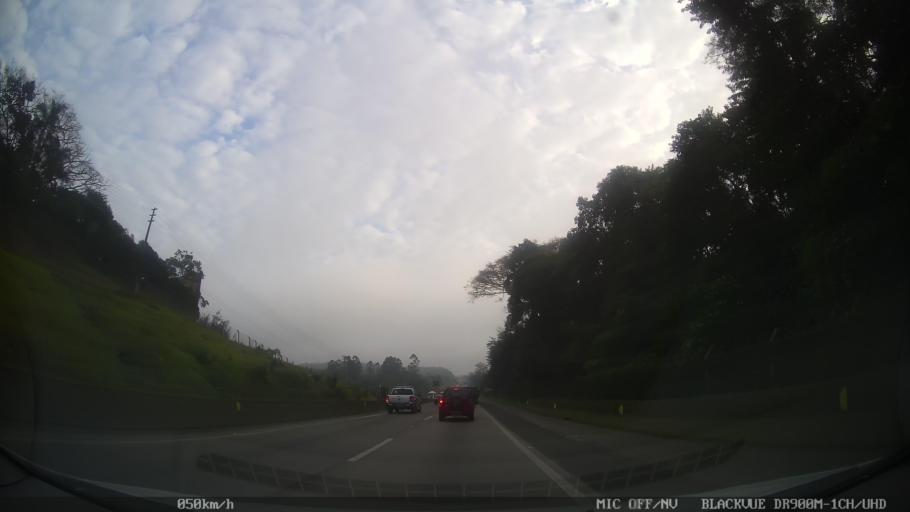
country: BR
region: Santa Catarina
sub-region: Penha
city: Penha
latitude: -26.7957
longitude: -48.6803
